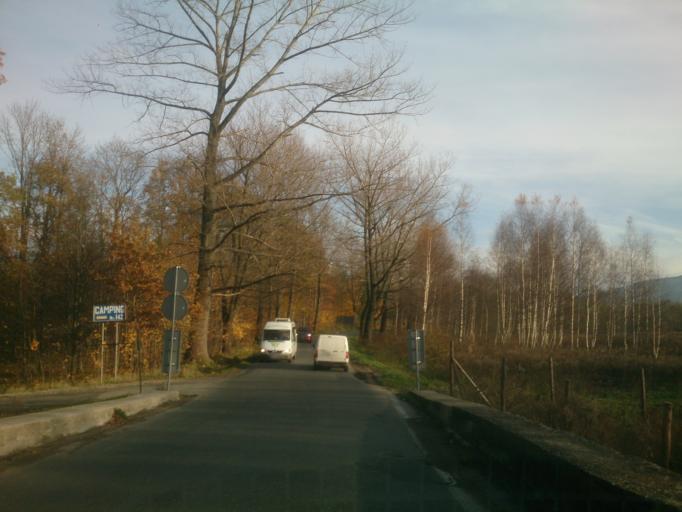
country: PL
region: Lower Silesian Voivodeship
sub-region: Powiat jeleniogorski
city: Karpacz
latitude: 50.8043
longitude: 15.7675
